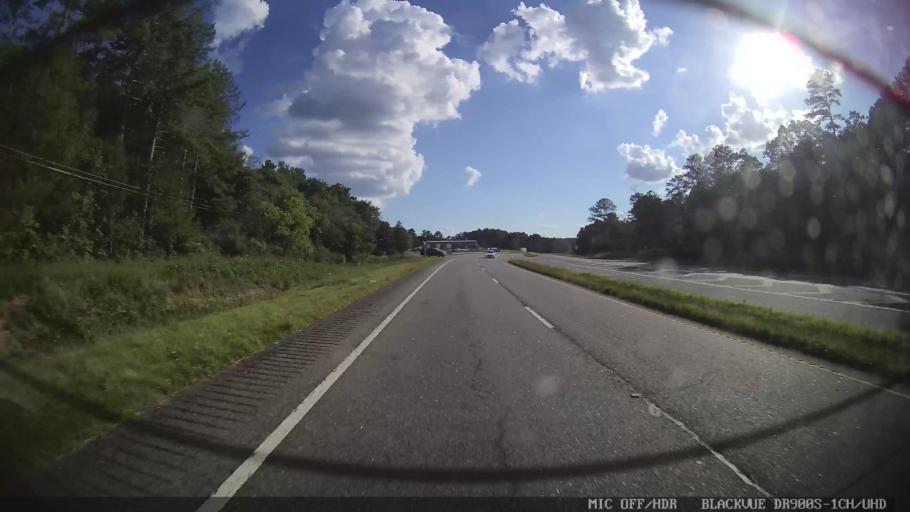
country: US
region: Georgia
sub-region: Bartow County
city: Euharlee
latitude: 34.2031
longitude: -84.9959
